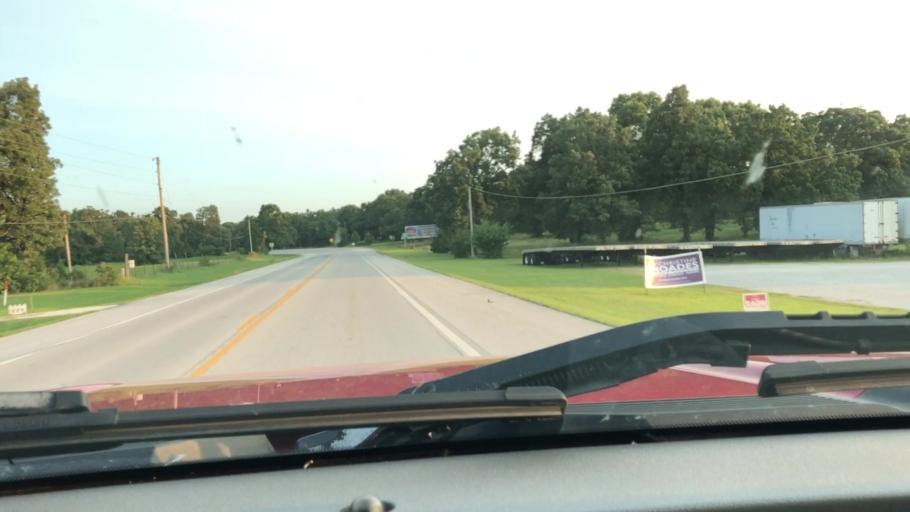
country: US
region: Missouri
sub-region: Jasper County
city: Duquesne
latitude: 36.9824
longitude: -94.4641
